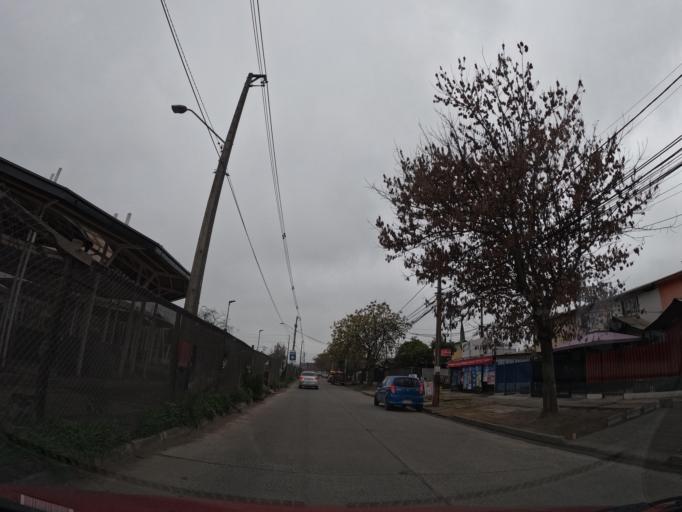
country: CL
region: Maule
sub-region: Provincia de Talca
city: Talca
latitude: -35.4395
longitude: -71.6323
